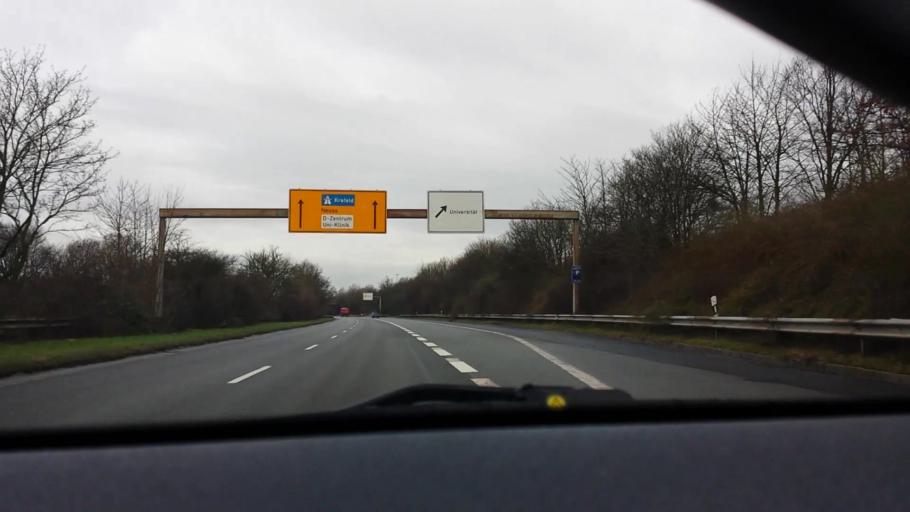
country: DE
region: North Rhine-Westphalia
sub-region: Regierungsbezirk Dusseldorf
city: Dusseldorf
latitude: 51.1792
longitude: 6.8060
